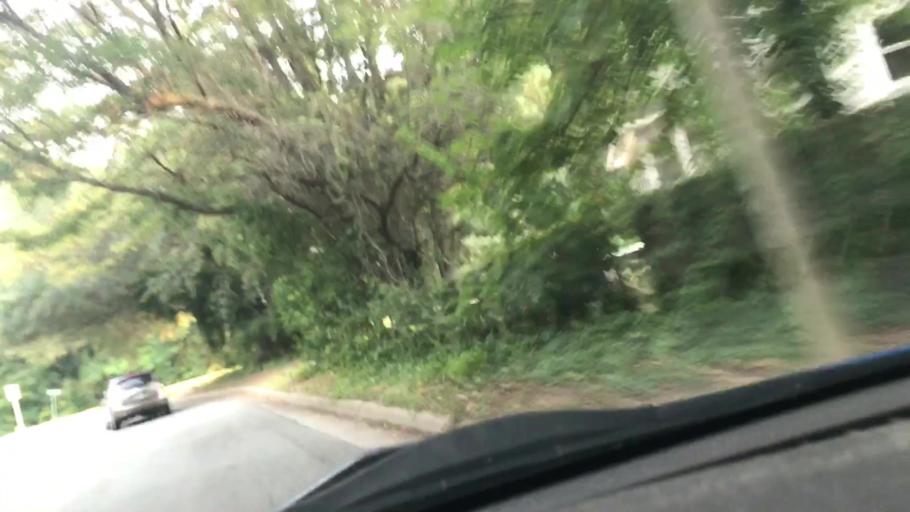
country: US
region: North Carolina
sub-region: Guilford County
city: Greensboro
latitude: 36.0744
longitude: -79.8096
